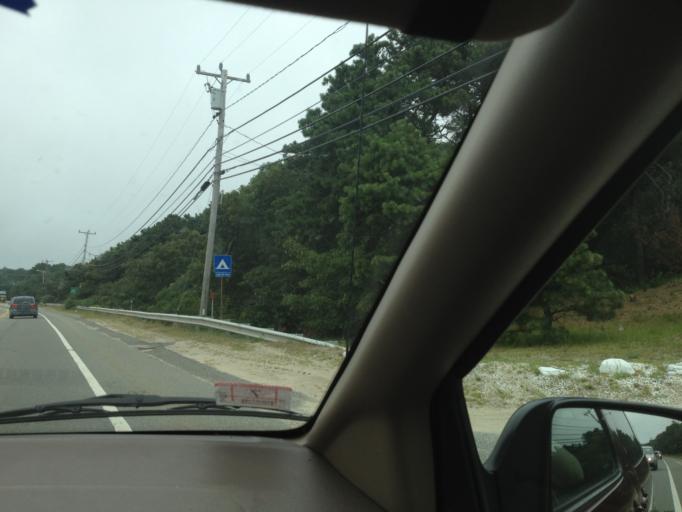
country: US
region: Massachusetts
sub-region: Barnstable County
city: North Eastham
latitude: 41.9130
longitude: -69.9870
